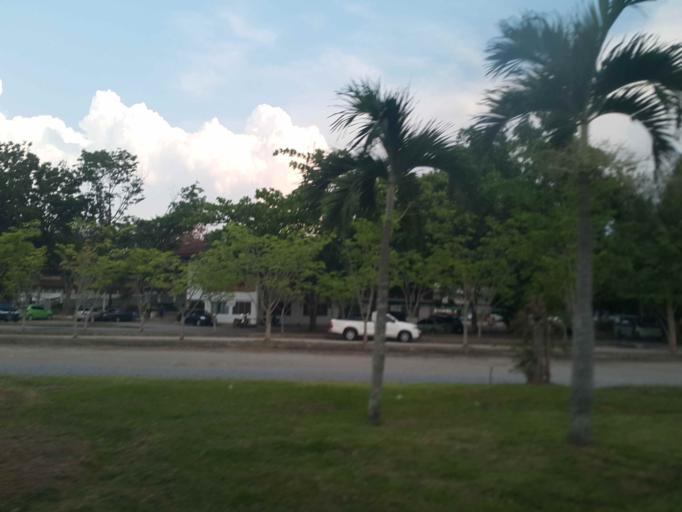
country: TH
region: Chiang Mai
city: Chiang Mai
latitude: 18.7952
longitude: 99.0305
